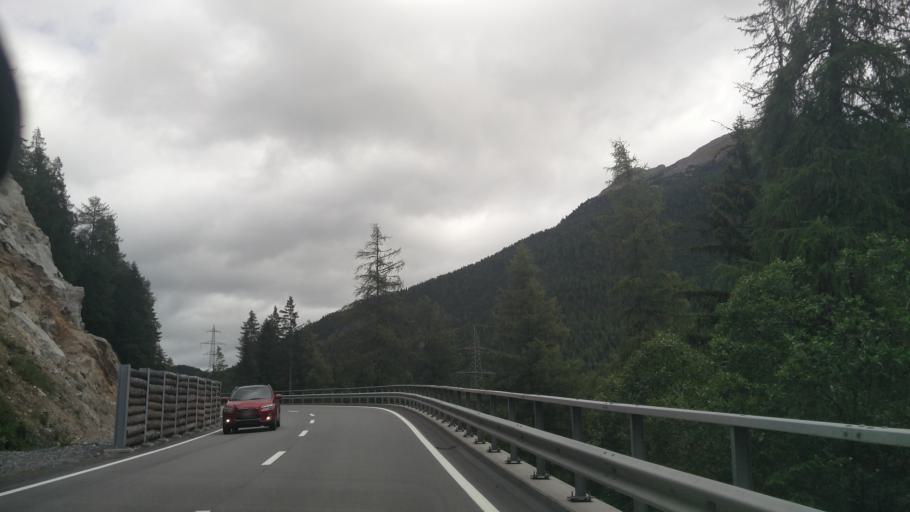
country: CH
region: Grisons
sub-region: Inn District
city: Zernez
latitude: 46.6959
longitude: 10.1173
